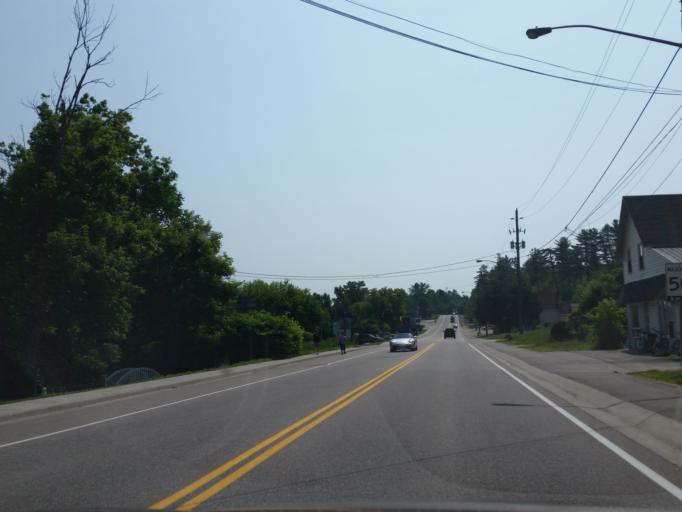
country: CA
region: Ontario
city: Mattawa
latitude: 46.3165
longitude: -78.6969
